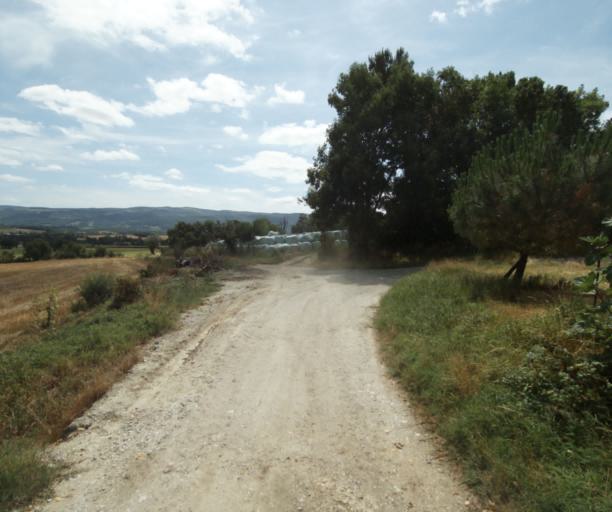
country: FR
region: Midi-Pyrenees
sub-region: Departement du Tarn
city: Soreze
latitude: 43.4916
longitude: 2.0687
